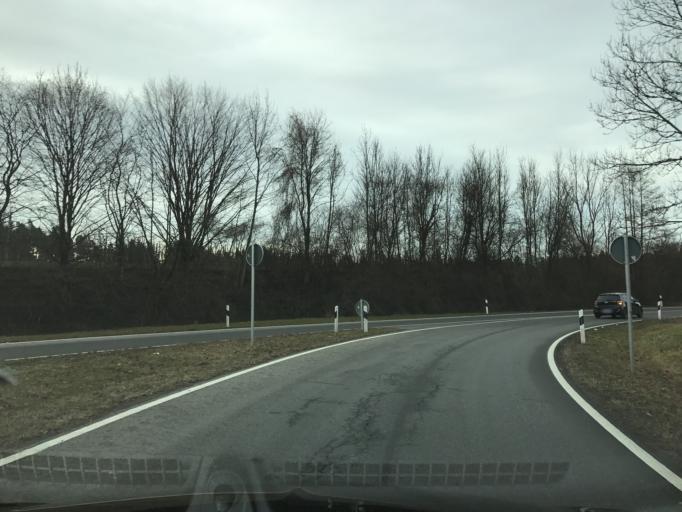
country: DE
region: Bavaria
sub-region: Swabia
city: Weissensberg
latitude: 47.5752
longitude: 9.7121
